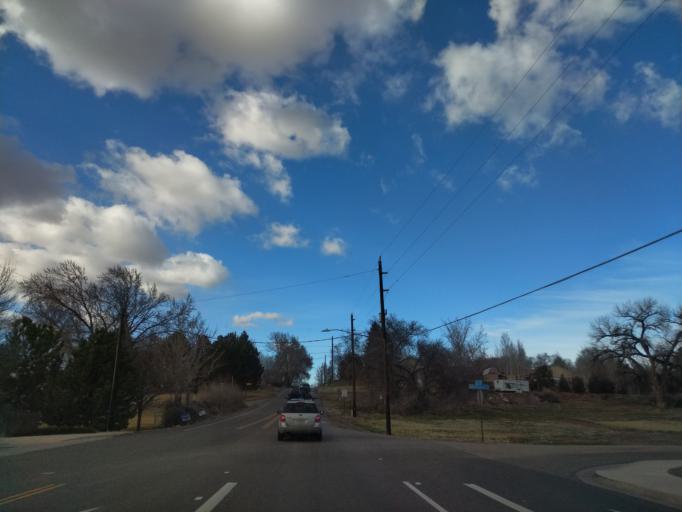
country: US
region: Colorado
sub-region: Mesa County
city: Grand Junction
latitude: 39.0925
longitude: -108.5708
